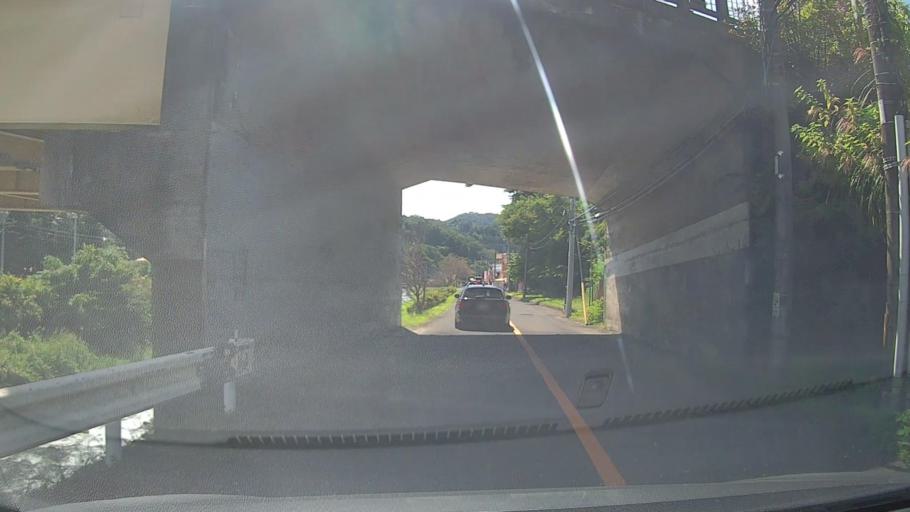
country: JP
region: Kanagawa
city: Hadano
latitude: 35.3787
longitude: 139.1706
